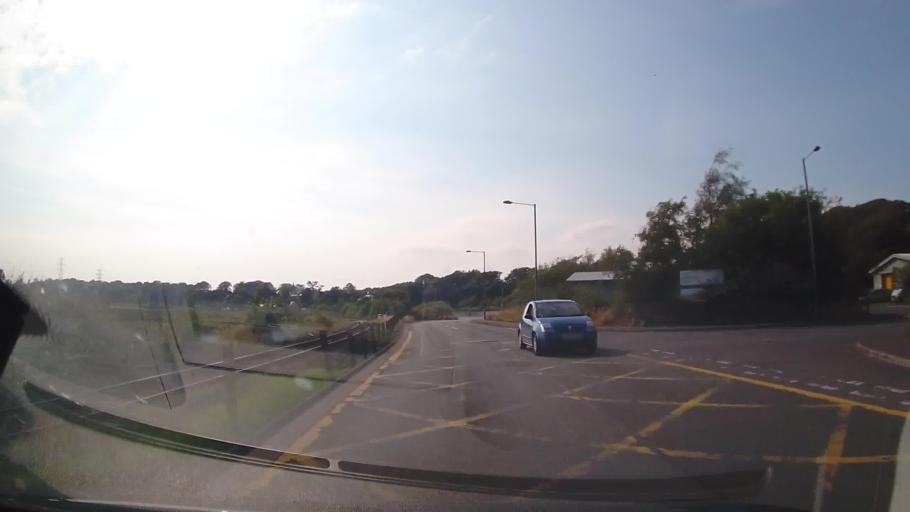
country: GB
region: Wales
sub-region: Gwynedd
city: Penrhyndeudraeth
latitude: 52.9290
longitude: -4.0595
